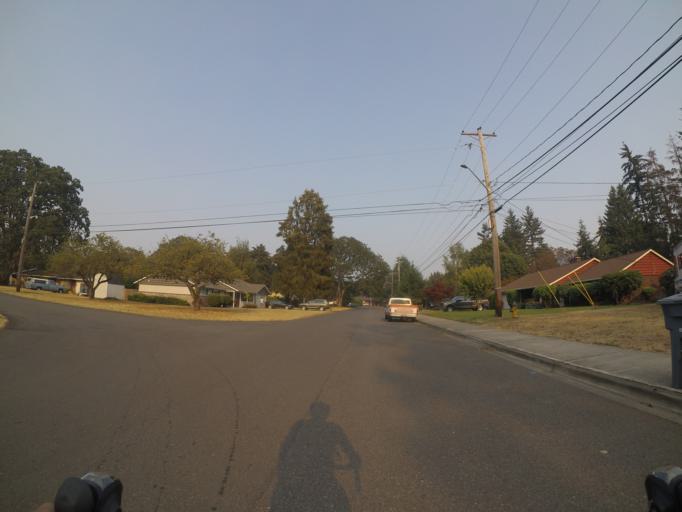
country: US
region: Washington
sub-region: Pierce County
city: Lakewood
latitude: 47.1795
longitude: -122.5158
